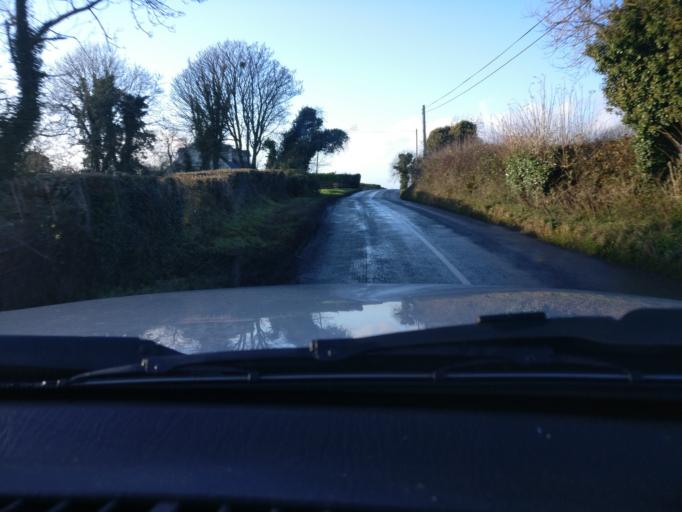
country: IE
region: Leinster
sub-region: An Mhi
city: Athboy
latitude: 53.6964
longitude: -7.0065
